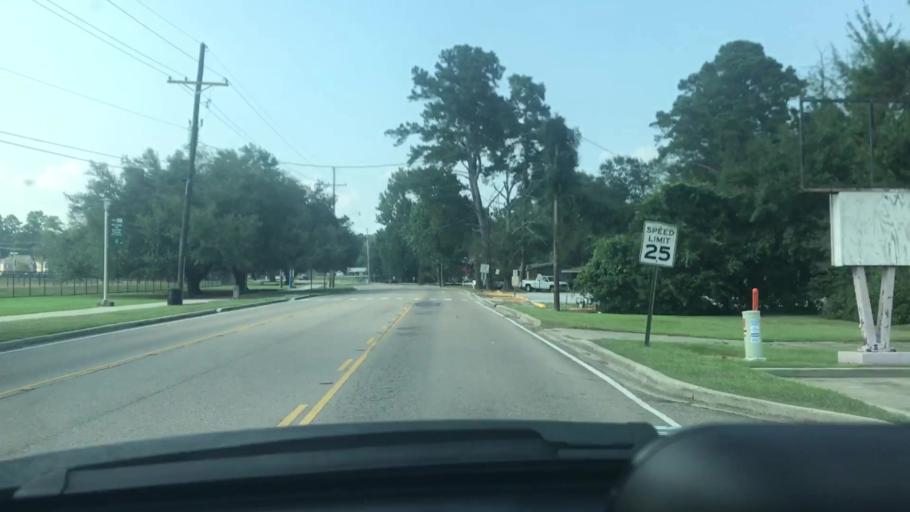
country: US
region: Louisiana
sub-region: Tangipahoa Parish
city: Hammond
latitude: 30.5164
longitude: -90.4657
